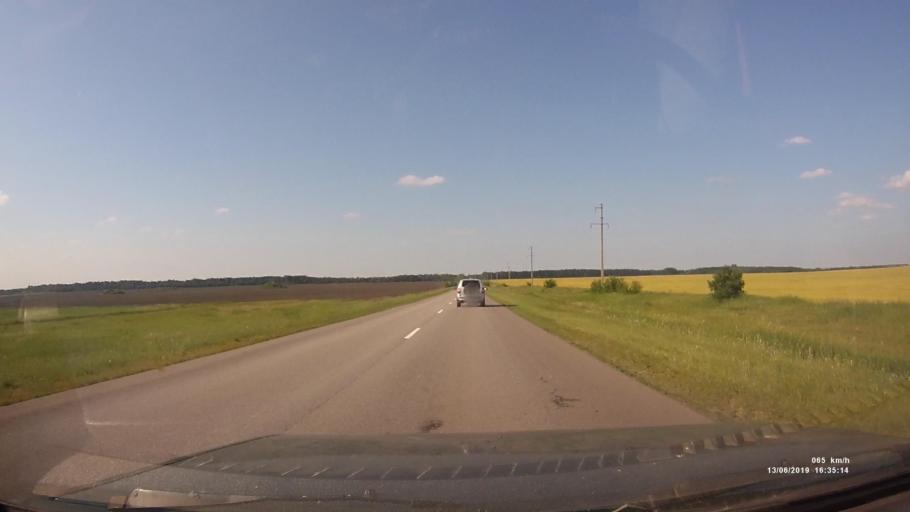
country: RU
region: Rostov
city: Kazanskaya
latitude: 49.8804
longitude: 41.2972
